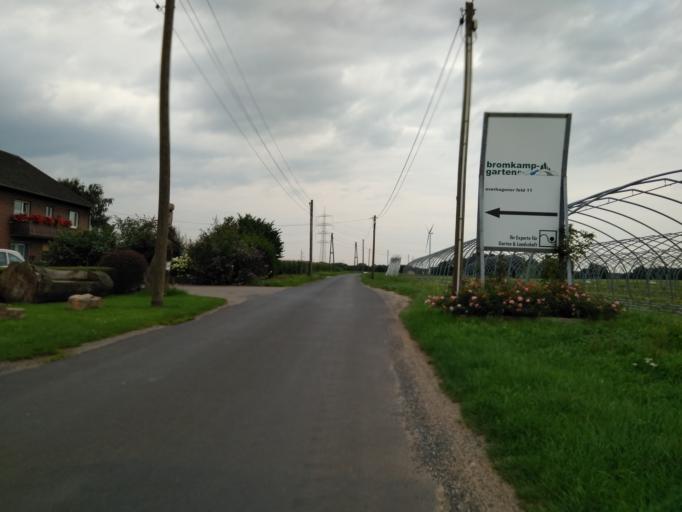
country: DE
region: North Rhine-Westphalia
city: Dorsten
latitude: 51.6159
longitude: 6.9451
